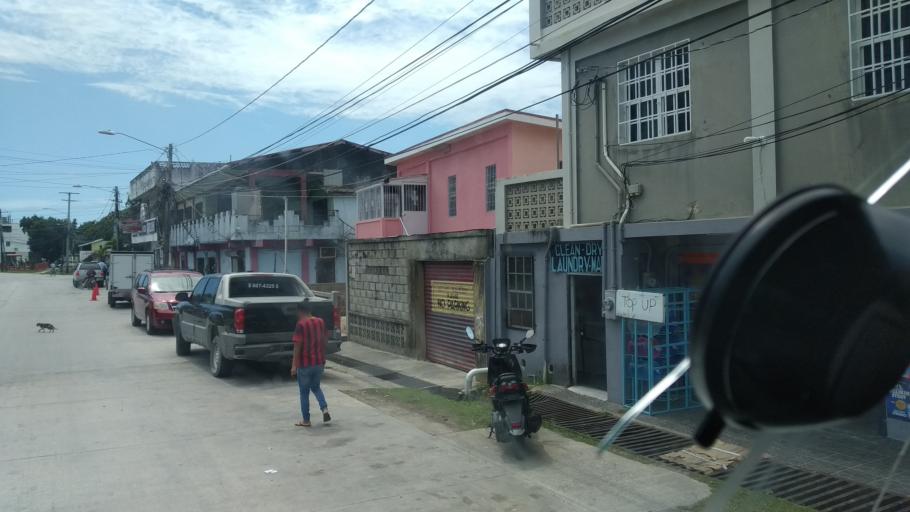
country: BZ
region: Belize
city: Belize City
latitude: 17.5051
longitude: -88.1902
